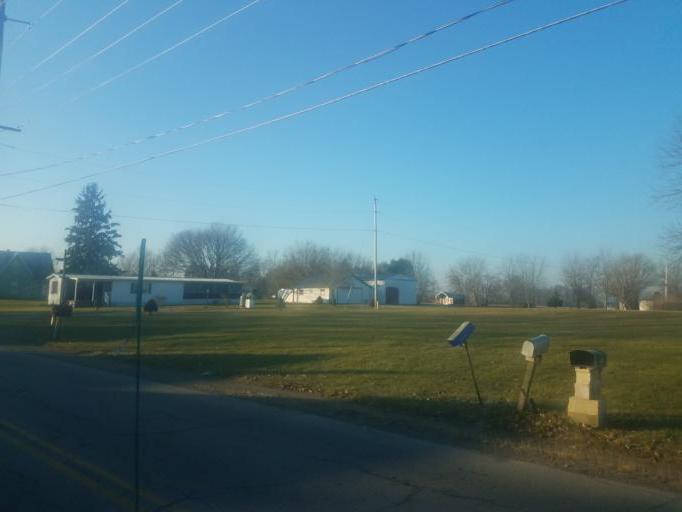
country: US
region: Ohio
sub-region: Crawford County
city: Bucyrus
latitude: 40.8210
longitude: -82.9819
